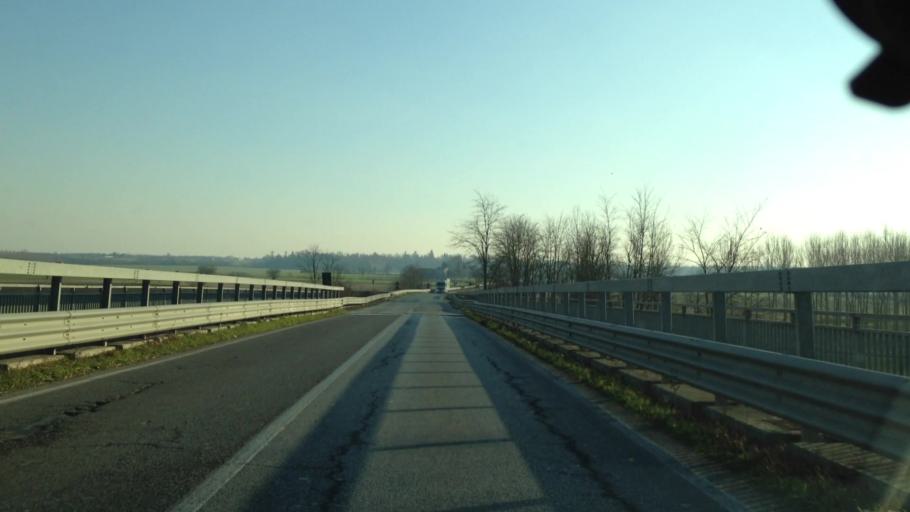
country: IT
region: Piedmont
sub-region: Provincia di Alessandria
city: Felizzano
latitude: 44.8898
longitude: 8.4393
